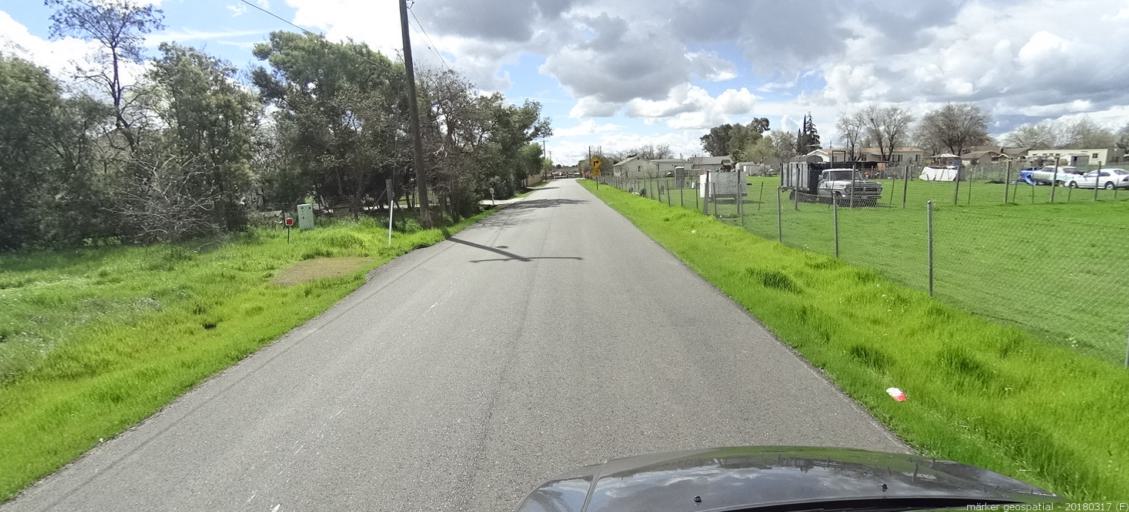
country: US
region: California
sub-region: Sacramento County
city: Florin
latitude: 38.4734
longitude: -121.4106
